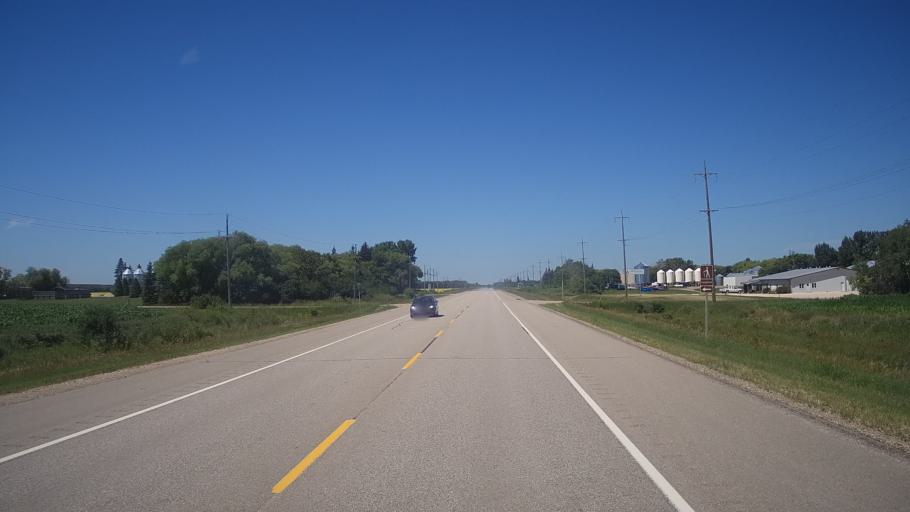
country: CA
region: Manitoba
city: Neepawa
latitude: 50.2252
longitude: -99.3151
